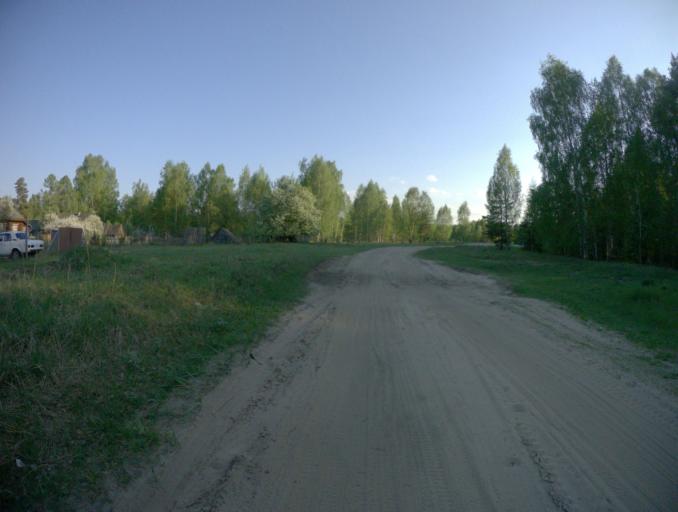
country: RU
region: Vladimir
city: Vyazniki
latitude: 56.3598
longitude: 42.1383
